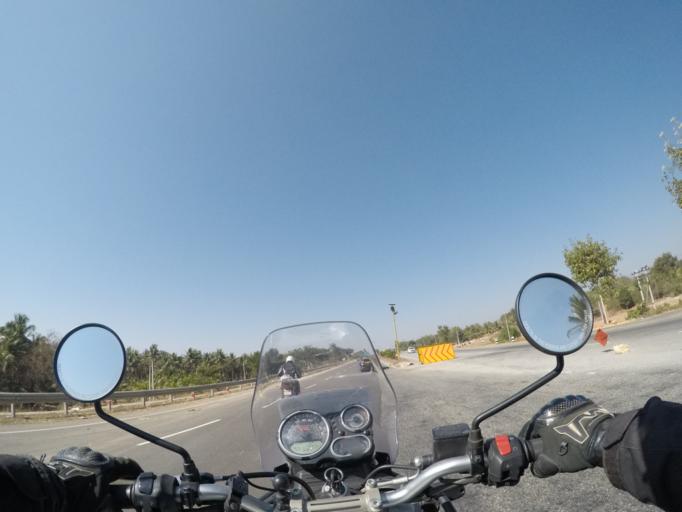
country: IN
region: Karnataka
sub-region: Mandya
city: Belluru
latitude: 12.9636
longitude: 76.7770
